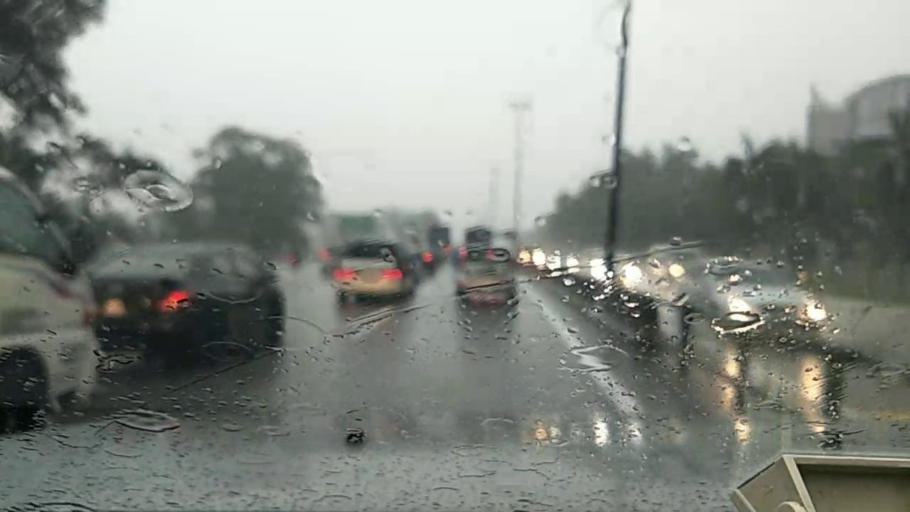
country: MY
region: Selangor
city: Kampong Baharu Balakong
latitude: 2.9808
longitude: 101.7395
